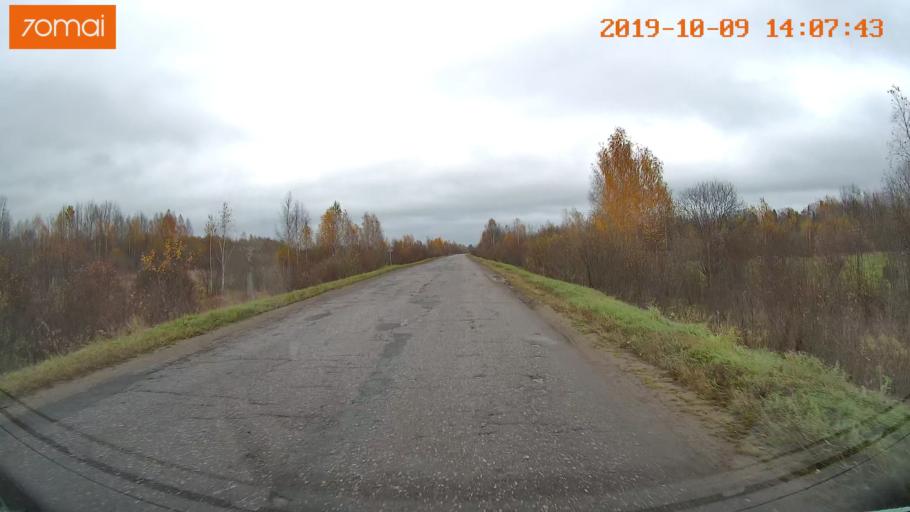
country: RU
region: Kostroma
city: Buy
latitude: 58.4724
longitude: 41.4264
